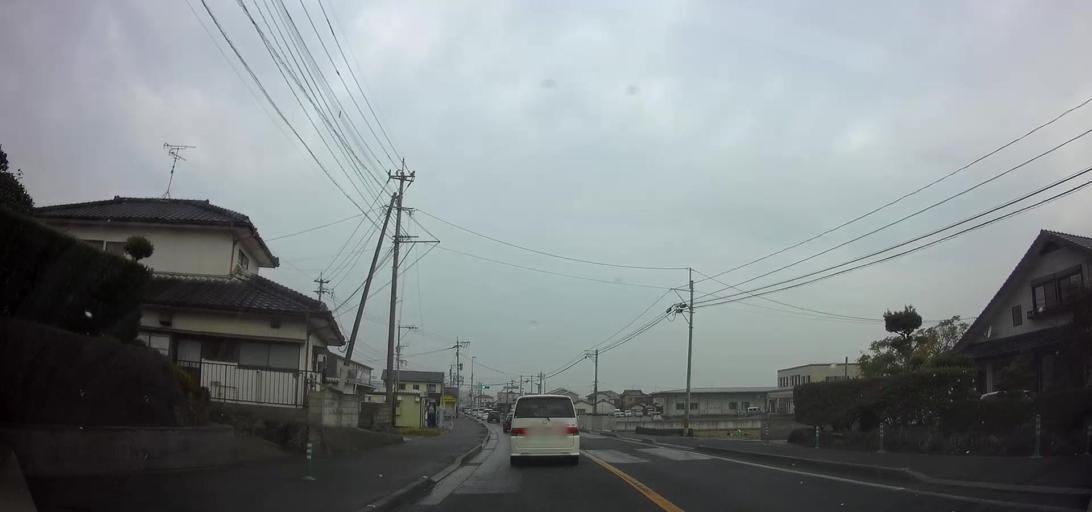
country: JP
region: Nagasaki
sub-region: Isahaya-shi
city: Isahaya
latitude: 32.8339
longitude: 130.1340
